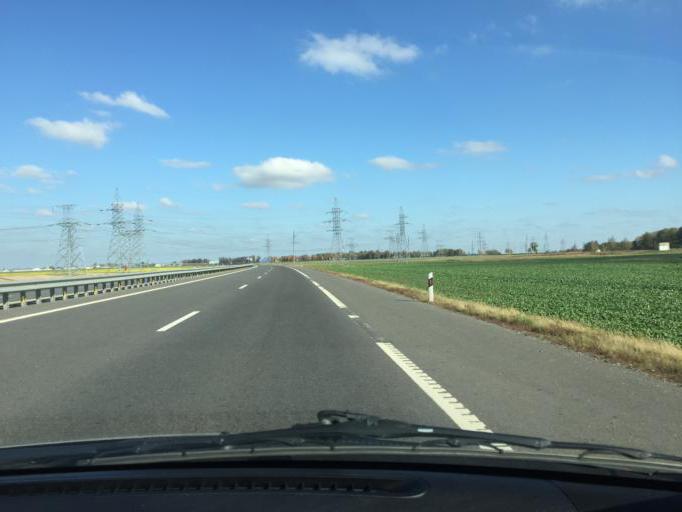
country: BY
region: Minsk
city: Slutsk
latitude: 53.0536
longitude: 27.5375
